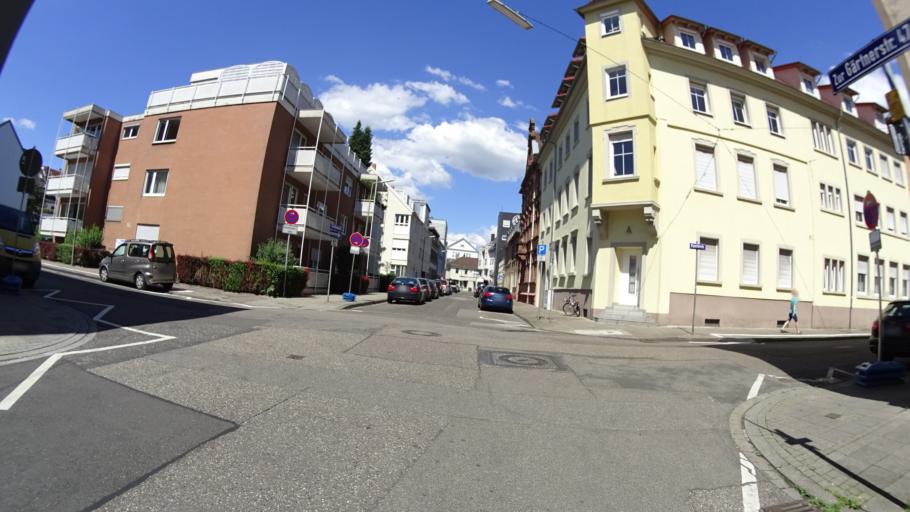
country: DE
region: Baden-Wuerttemberg
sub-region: Karlsruhe Region
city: Karlsruhe
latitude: 48.9984
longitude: 8.4661
